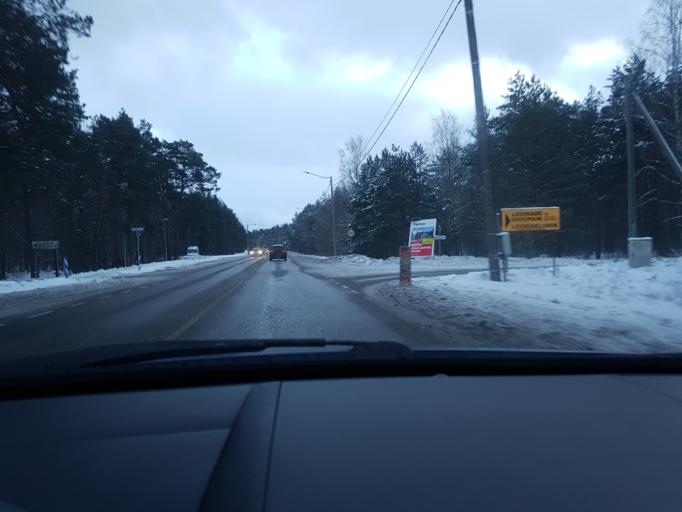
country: EE
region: Harju
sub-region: Tallinna linn
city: Tallinn
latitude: 59.3711
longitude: 24.7523
